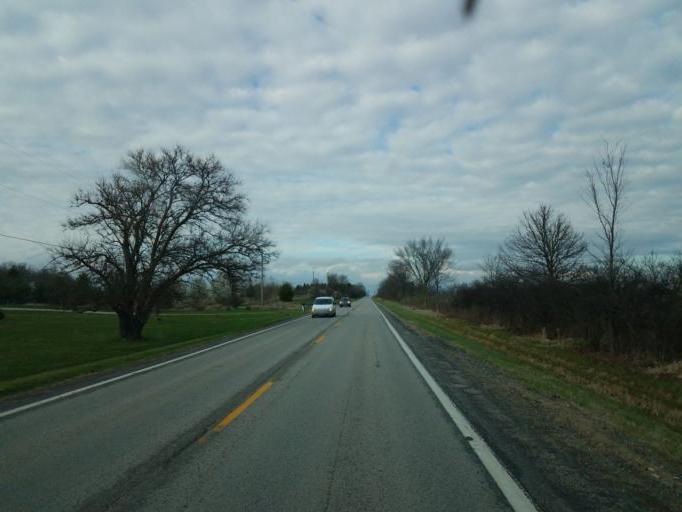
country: US
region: Ohio
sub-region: Delaware County
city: Ashley
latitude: 40.3498
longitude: -82.9940
